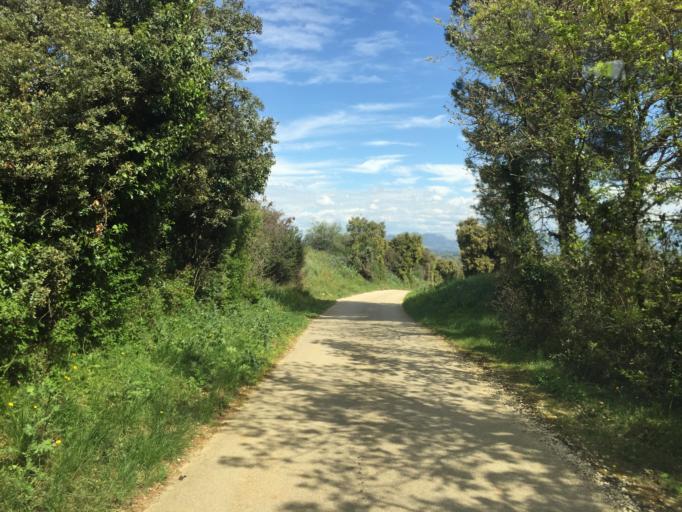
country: FR
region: Provence-Alpes-Cote d'Azur
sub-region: Departement du Vaucluse
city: Courthezon
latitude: 44.0658
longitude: 4.8650
